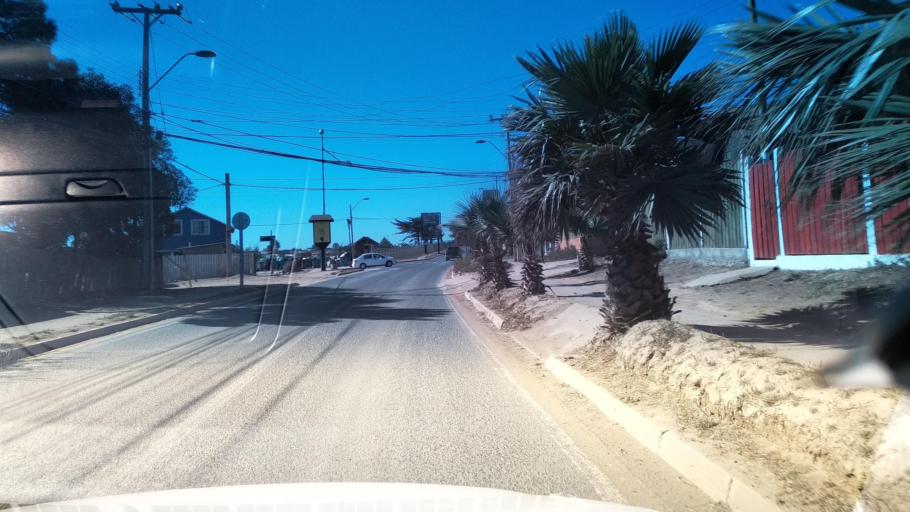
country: CL
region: O'Higgins
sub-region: Provincia de Colchagua
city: Santa Cruz
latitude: -34.3998
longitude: -72.0229
